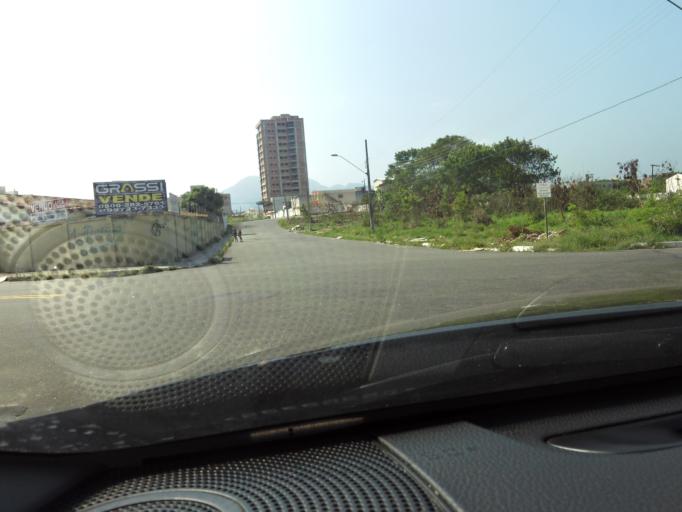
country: BR
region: Espirito Santo
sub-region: Guarapari
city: Guarapari
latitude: -20.6501
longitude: -40.4841
